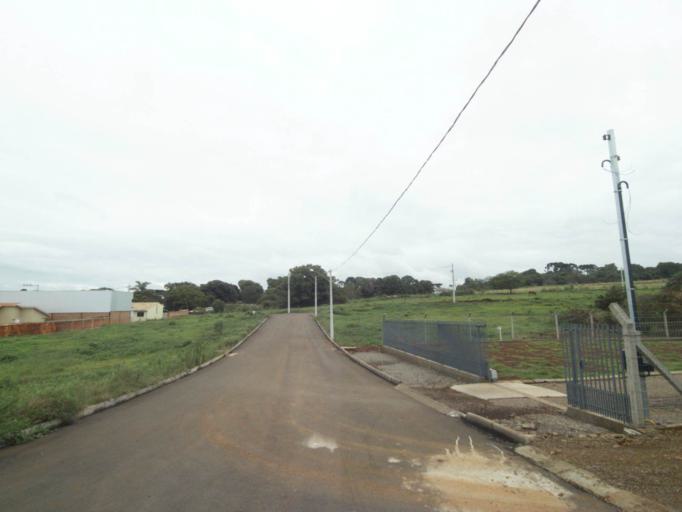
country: BR
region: Rio Grande do Sul
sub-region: Lagoa Vermelha
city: Lagoa Vermelha
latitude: -28.2214
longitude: -51.5202
